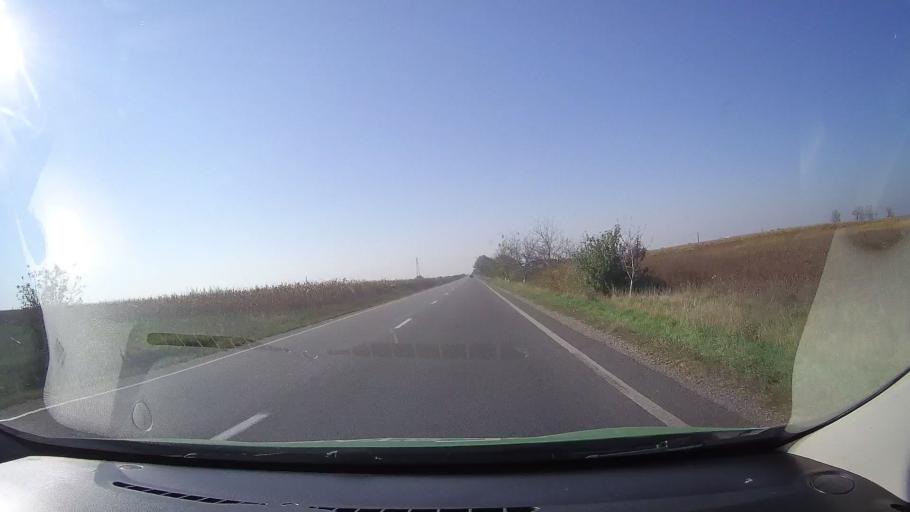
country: RO
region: Satu Mare
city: Carei
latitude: 47.6668
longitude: 22.4363
